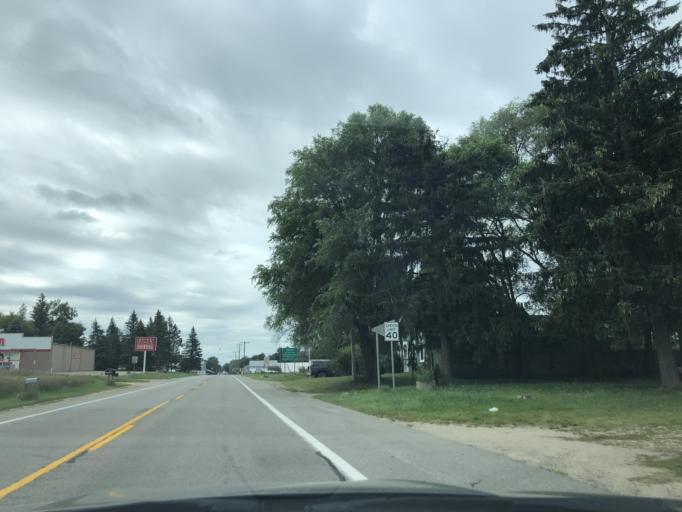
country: US
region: Michigan
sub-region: Missaukee County
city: Lake City
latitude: 44.1103
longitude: -85.1476
